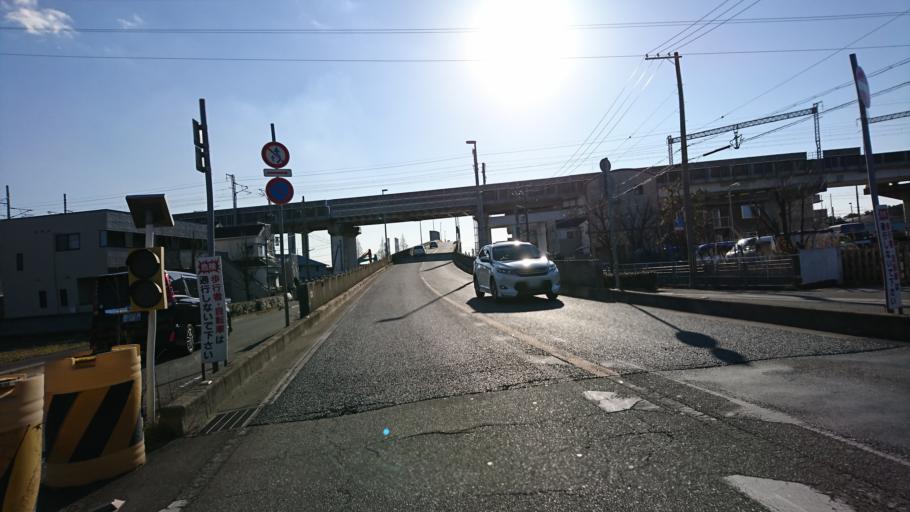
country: JP
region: Hyogo
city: Kakogawacho-honmachi
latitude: 34.7377
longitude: 134.8420
